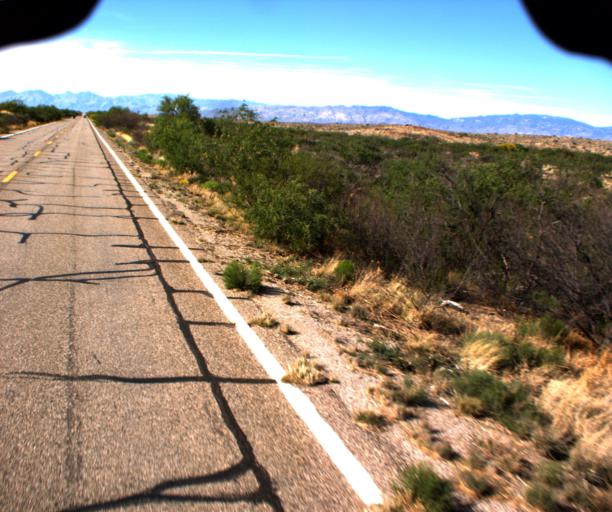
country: US
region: Arizona
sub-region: Pima County
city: Vail
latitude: 31.9553
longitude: -110.6687
